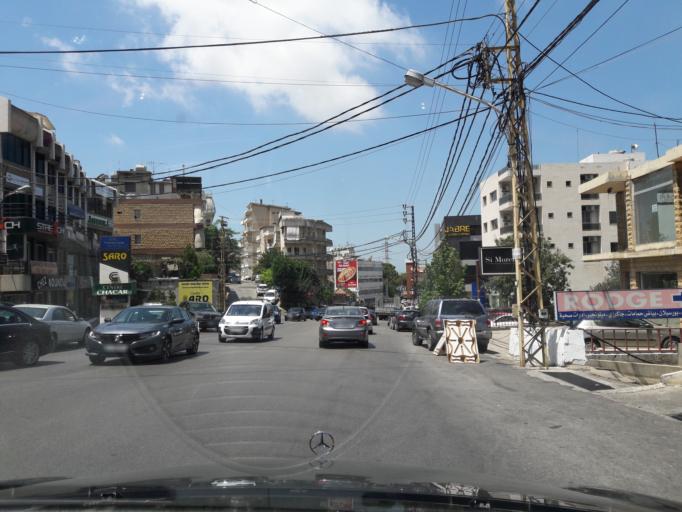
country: LB
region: Mont-Liban
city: Djounie
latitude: 33.9262
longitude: 35.6295
